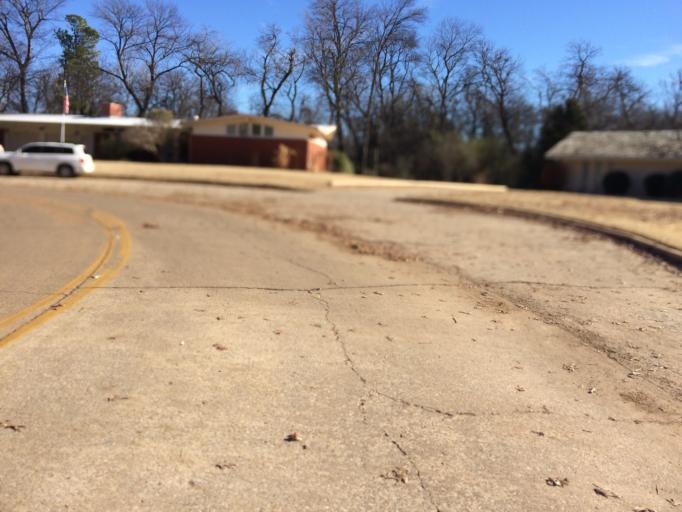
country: US
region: Oklahoma
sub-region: Cleveland County
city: Norman
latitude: 35.2124
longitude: -97.4310
